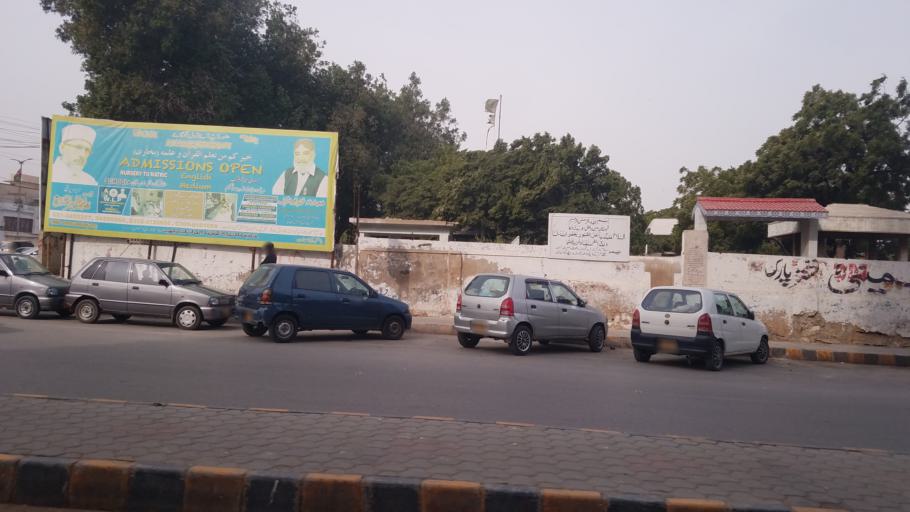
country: PK
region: Sindh
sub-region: Karachi District
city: Karachi
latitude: 24.8654
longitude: 67.0559
